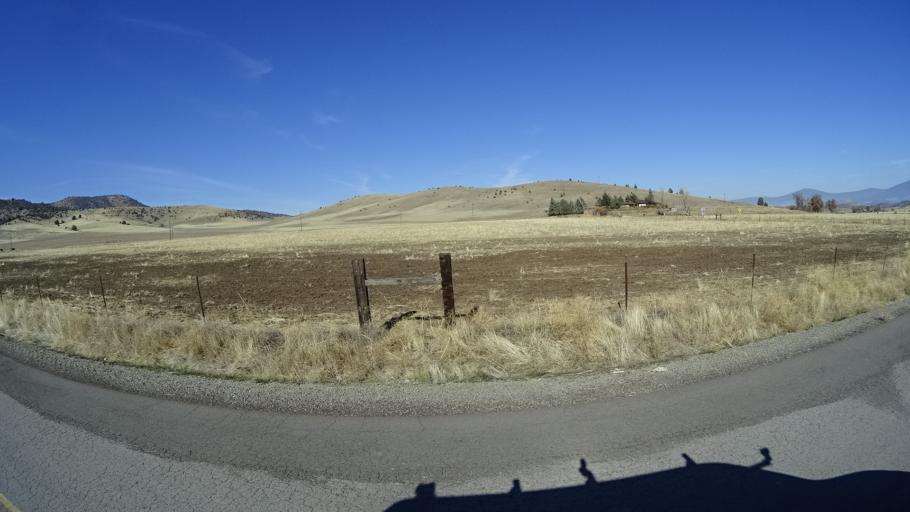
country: US
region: California
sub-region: Siskiyou County
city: Montague
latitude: 41.5971
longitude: -122.5357
